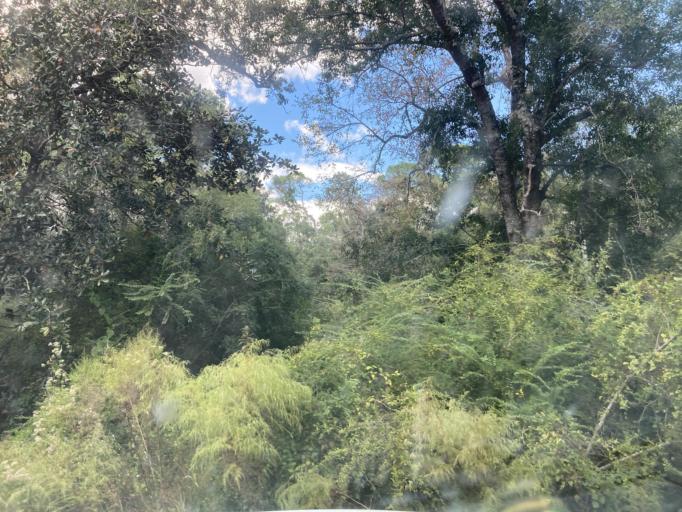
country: US
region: Mississippi
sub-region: Jackson County
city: Gulf Hills
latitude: 30.4446
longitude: -88.8368
